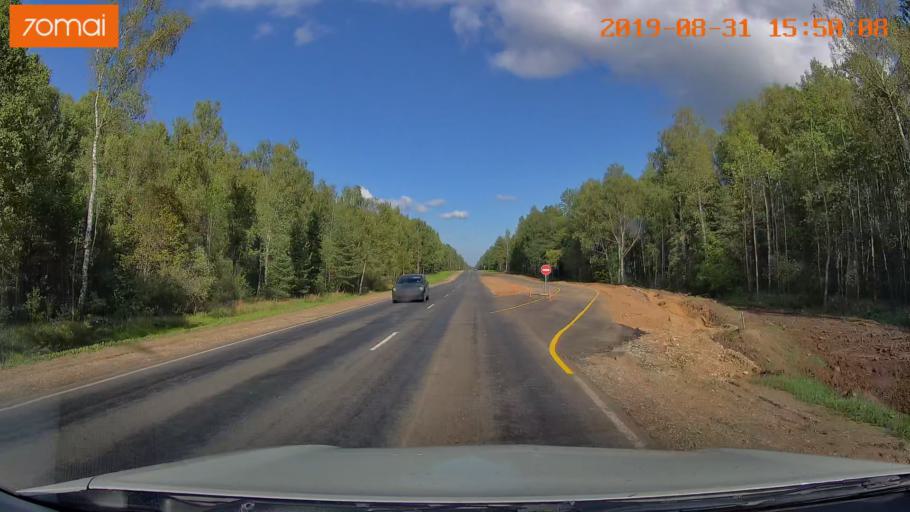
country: RU
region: Kaluga
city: Yukhnov
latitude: 54.6952
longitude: 35.0661
